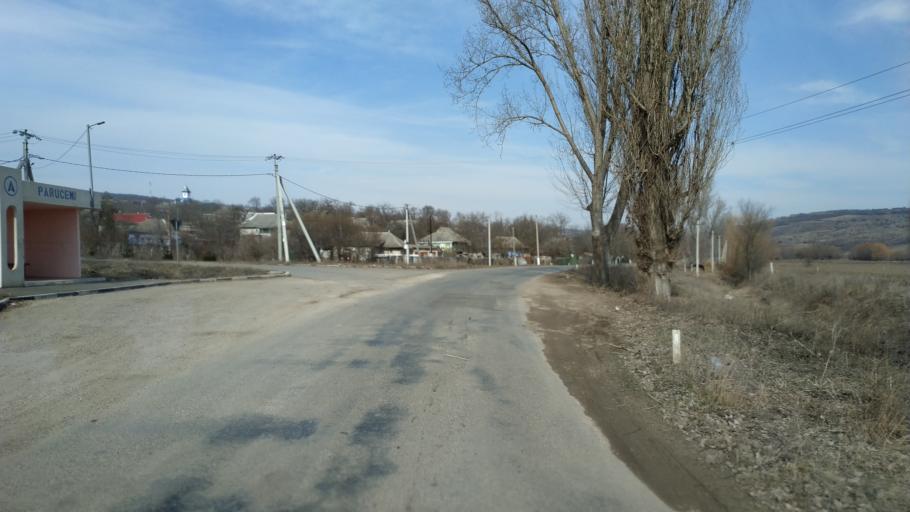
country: MD
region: Nisporeni
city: Nisporeni
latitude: 47.1490
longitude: 28.1081
